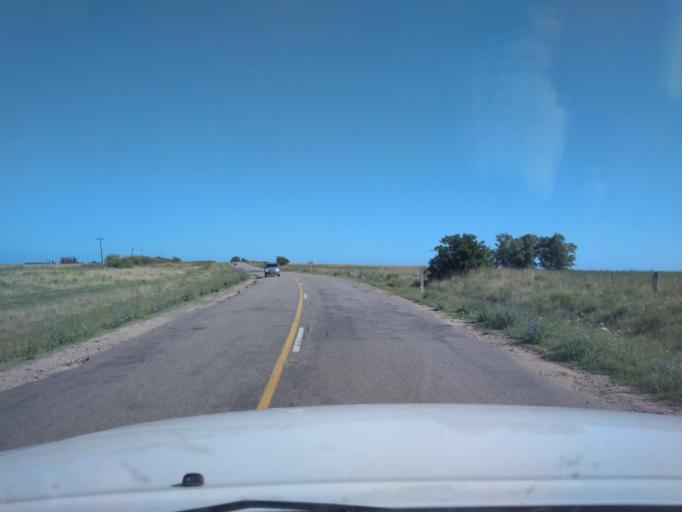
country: UY
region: Canelones
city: San Ramon
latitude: -34.2116
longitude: -55.9292
